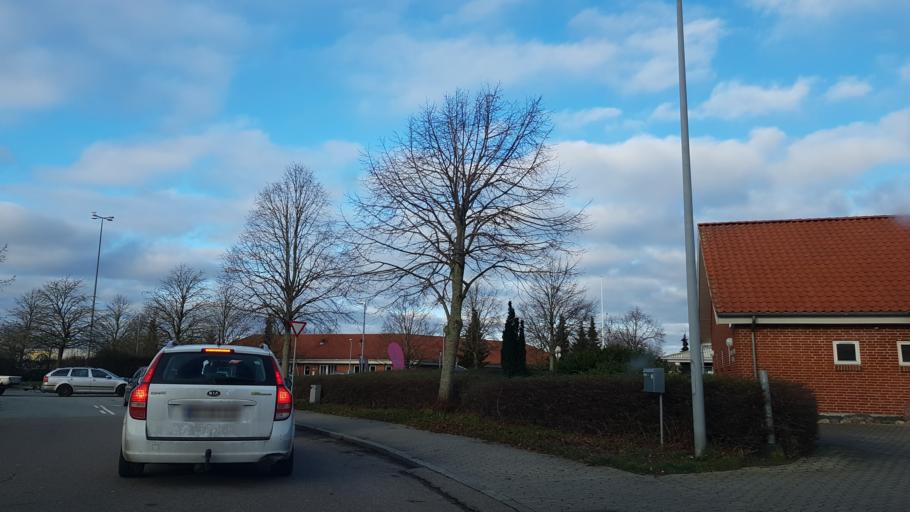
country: DK
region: Zealand
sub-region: Slagelse Kommune
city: Slagelse
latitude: 55.3886
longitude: 11.3298
